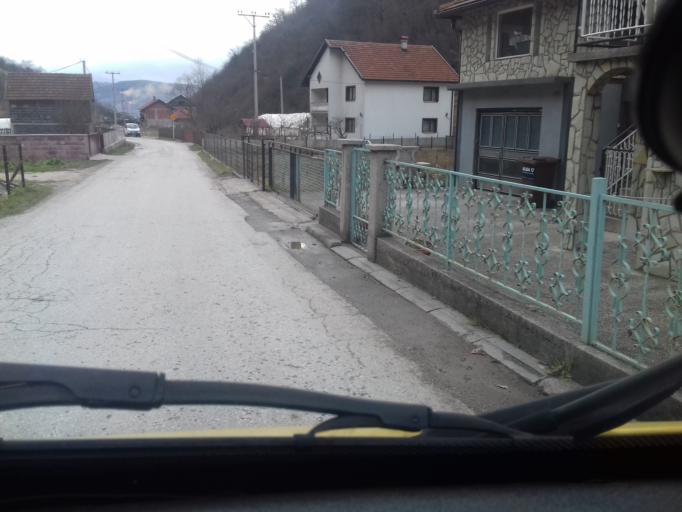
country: BA
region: Federation of Bosnia and Herzegovina
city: Zenica
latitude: 44.2487
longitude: 17.9213
